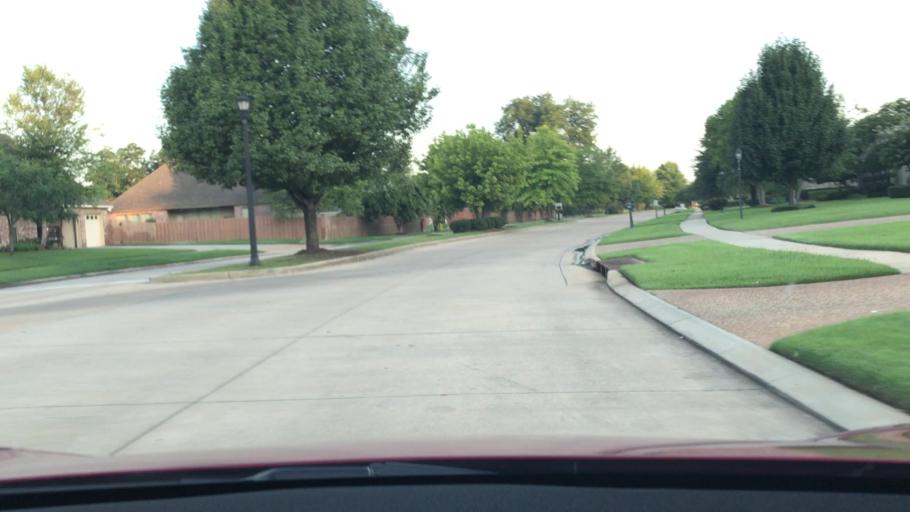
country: US
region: Louisiana
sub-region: Bossier Parish
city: Bossier City
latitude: 32.3979
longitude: -93.7086
